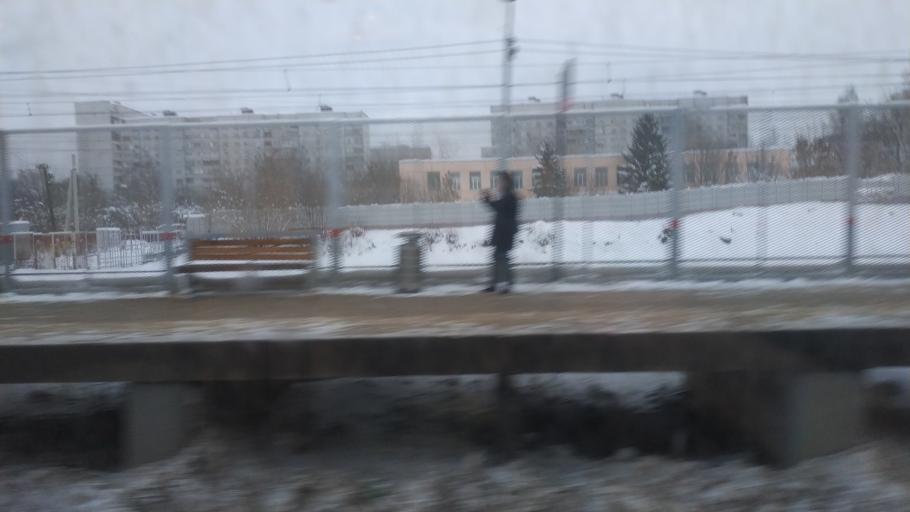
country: RU
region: Moskovskaya
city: Shcherbinka
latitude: 55.5407
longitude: 37.5705
